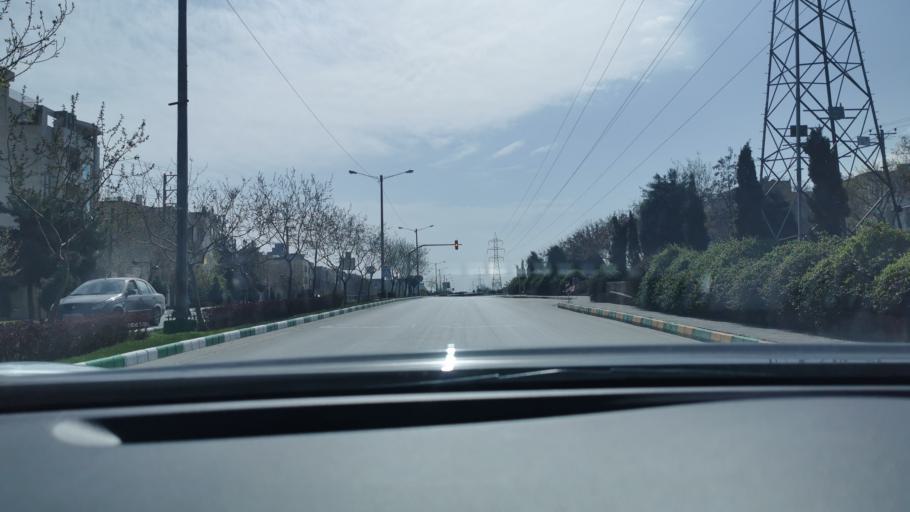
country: IR
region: Razavi Khorasan
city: Mashhad
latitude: 36.2889
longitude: 59.5331
